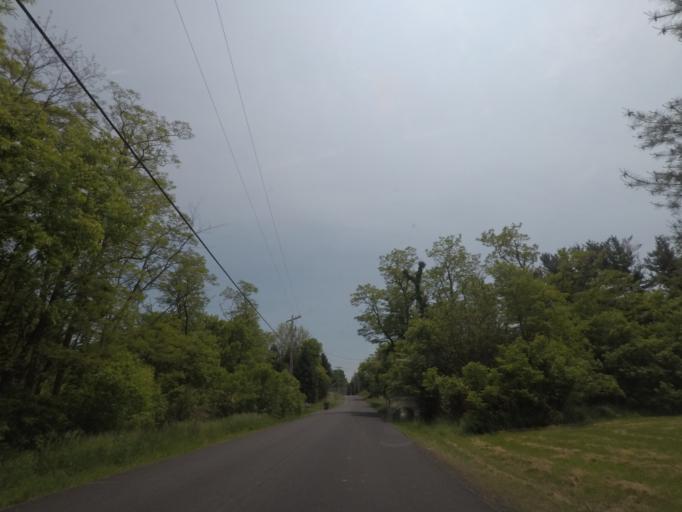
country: US
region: New York
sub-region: Rensselaer County
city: Castleton-on-Hudson
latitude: 42.5072
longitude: -73.7077
